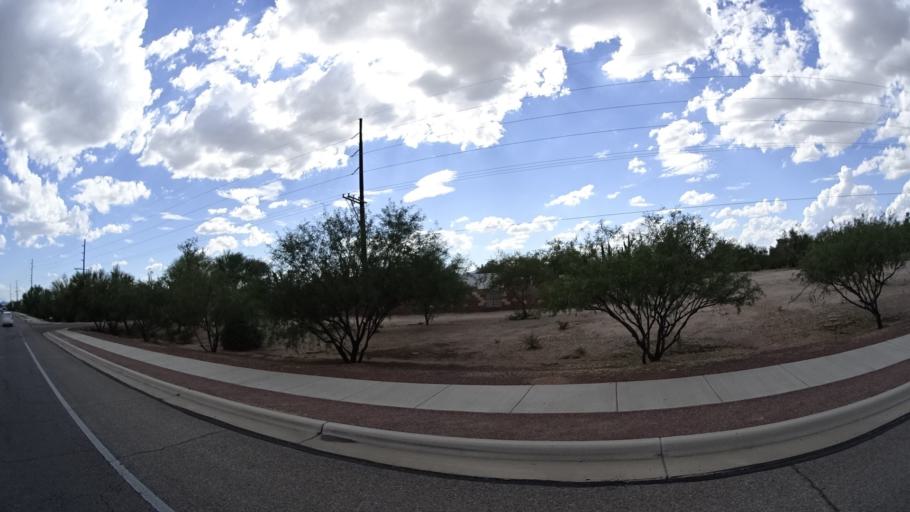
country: US
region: Arizona
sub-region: Pima County
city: Casas Adobes
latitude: 32.3284
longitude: -111.0129
